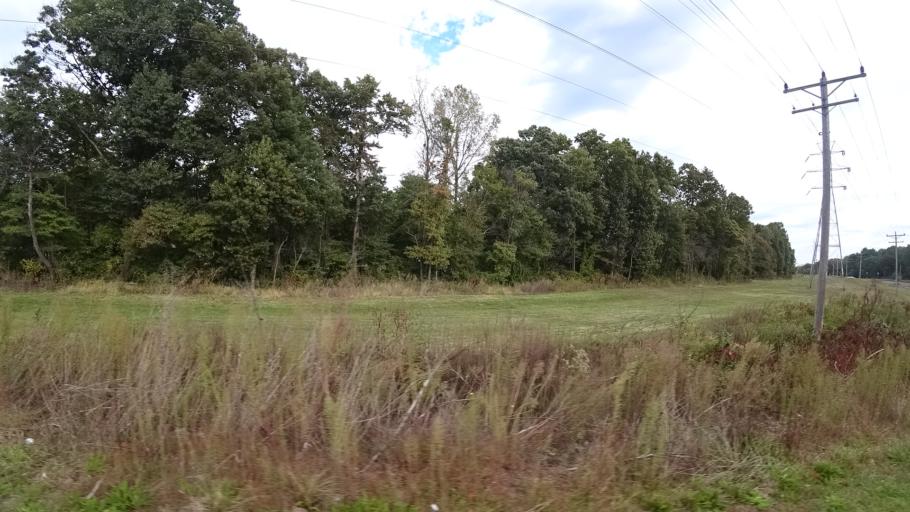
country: US
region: Indiana
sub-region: LaPorte County
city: Trail Creek
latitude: 41.7021
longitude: -86.8678
